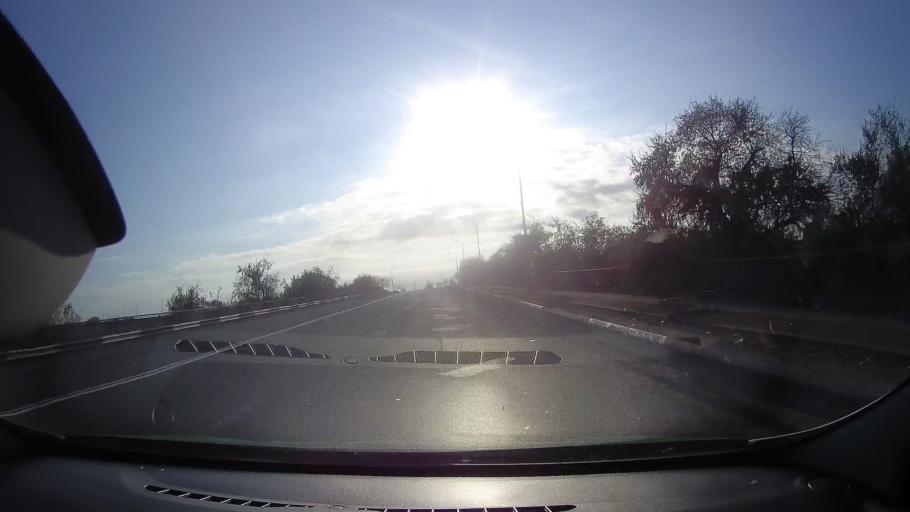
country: RO
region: Constanta
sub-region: Comuna Navodari
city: Navodari
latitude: 44.3242
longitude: 28.6236
